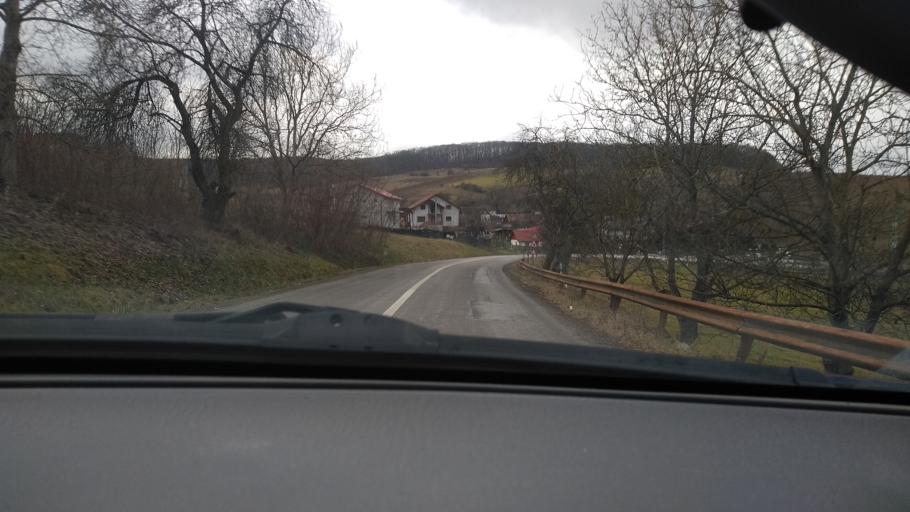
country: RO
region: Mures
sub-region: Comuna Pasareni
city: Pasareni
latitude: 46.5392
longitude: 24.6950
